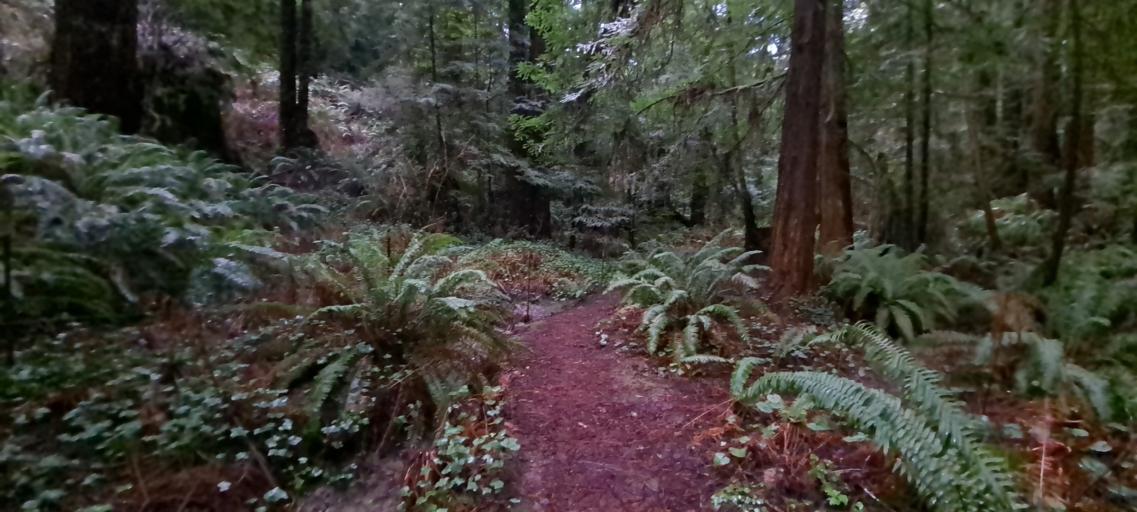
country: US
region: California
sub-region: Humboldt County
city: Fortuna
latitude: 40.6029
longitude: -124.1464
